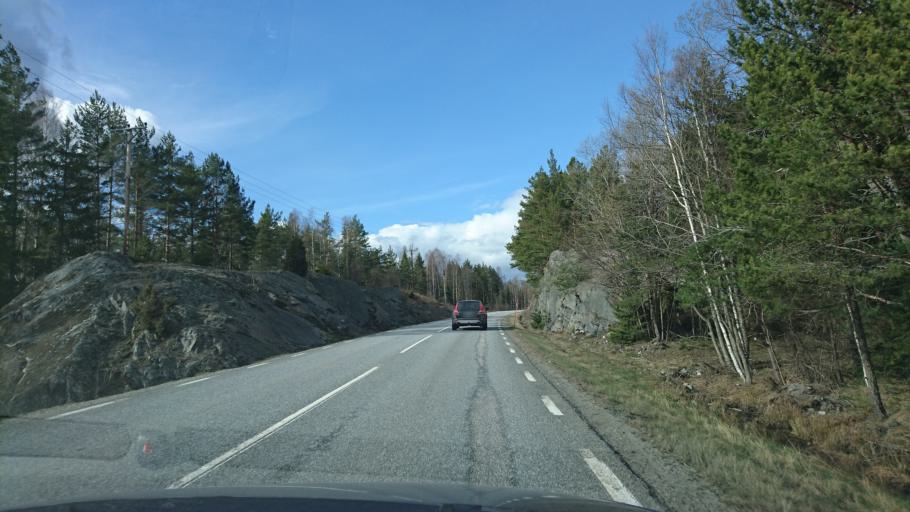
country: SE
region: Stockholm
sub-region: Nynashamns Kommun
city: Nynashamn
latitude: 58.9545
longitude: 17.9975
